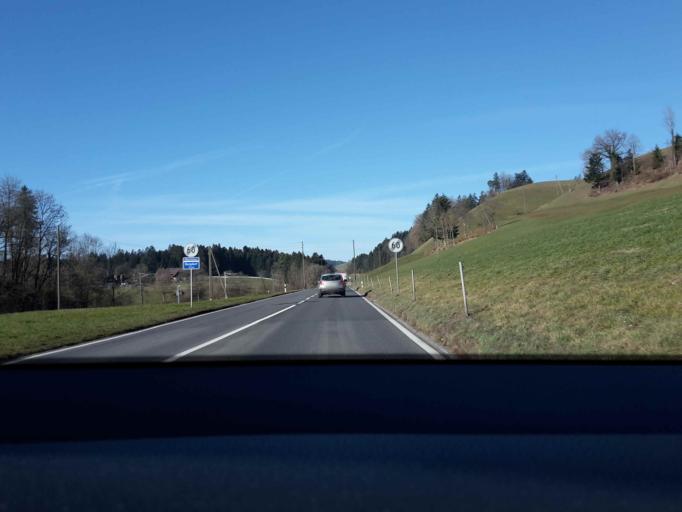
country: CH
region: Bern
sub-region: Emmental District
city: Durrenroth
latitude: 47.0920
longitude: 7.7900
